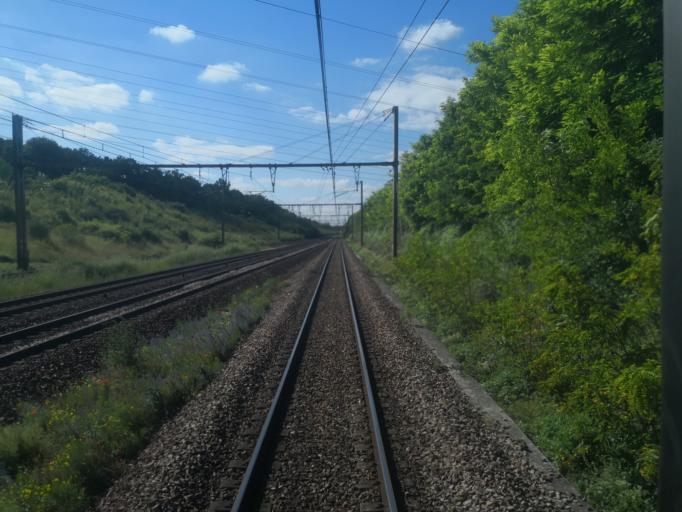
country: FR
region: Ile-de-France
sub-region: Departement de Seine-et-Marne
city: Le Mee-sur-Seine
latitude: 48.5412
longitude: 2.6222
